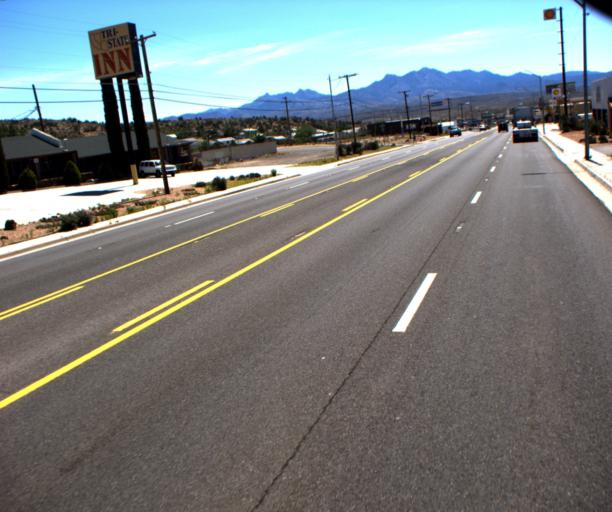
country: US
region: Arizona
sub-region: Mohave County
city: Kingman
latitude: 35.1962
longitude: -114.0752
